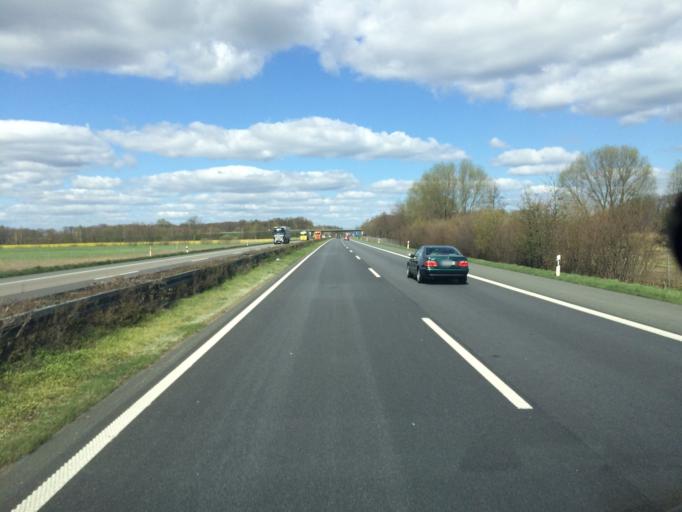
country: DE
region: North Rhine-Westphalia
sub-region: Regierungsbezirk Munster
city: Heek
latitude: 52.1659
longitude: 7.0982
